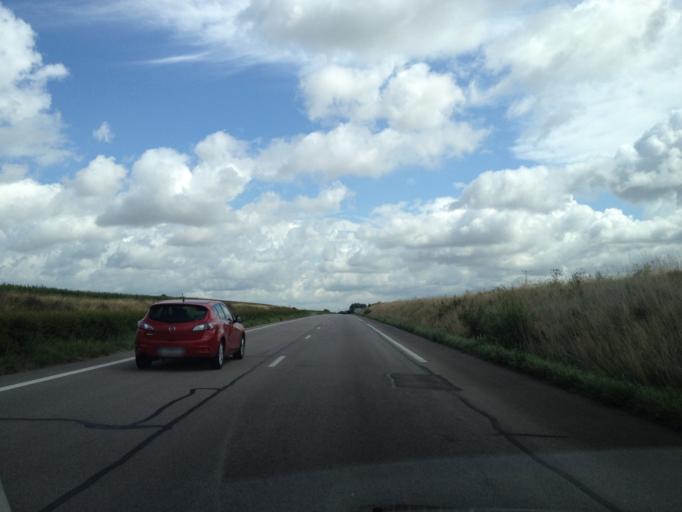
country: FR
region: Haute-Normandie
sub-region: Departement de la Seine-Maritime
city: Blainville-Crevon
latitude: 49.5535
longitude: 1.2554
